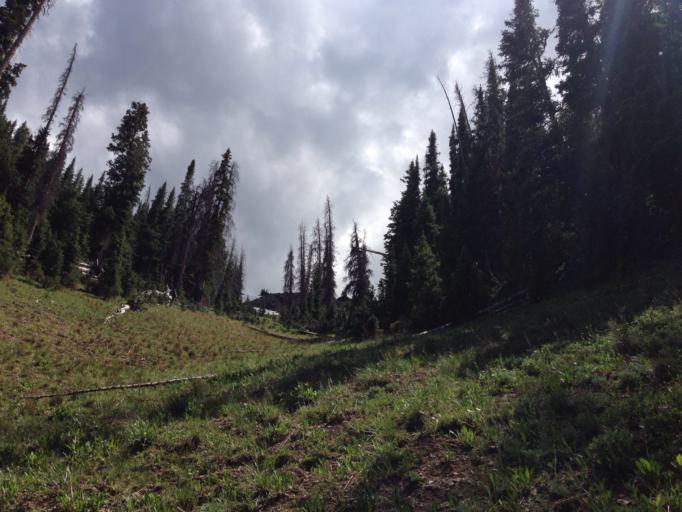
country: US
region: Colorado
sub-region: Larimer County
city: Estes Park
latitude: 40.4955
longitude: -105.8906
